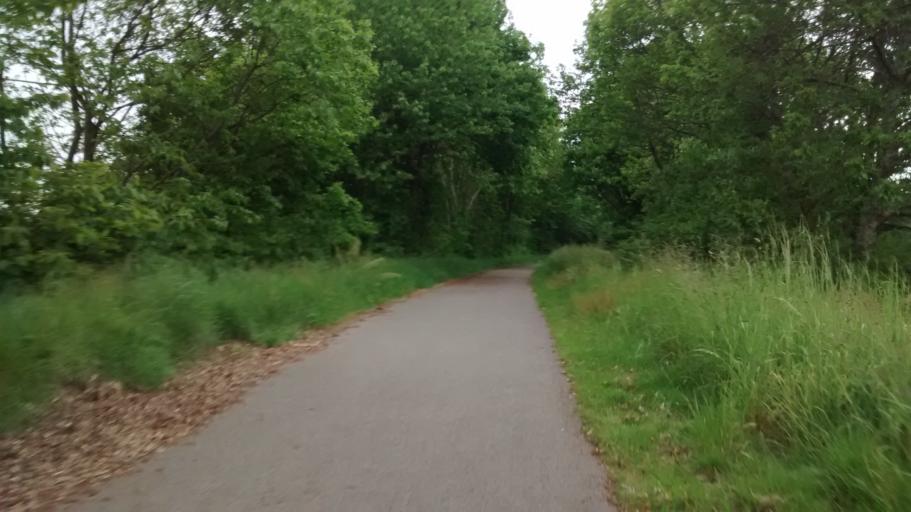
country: FR
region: Brittany
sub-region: Departement du Morbihan
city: Malestroit
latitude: 47.7891
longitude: -2.4015
